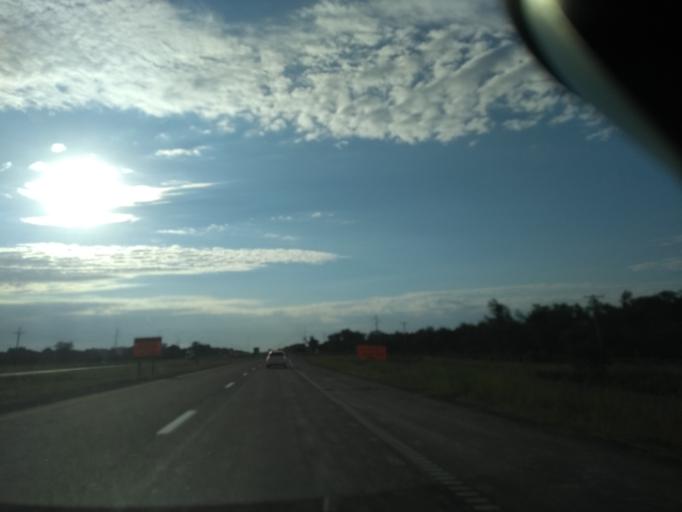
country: AR
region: Chaco
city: Puerto Tirol
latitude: -27.2726
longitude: -59.1416
